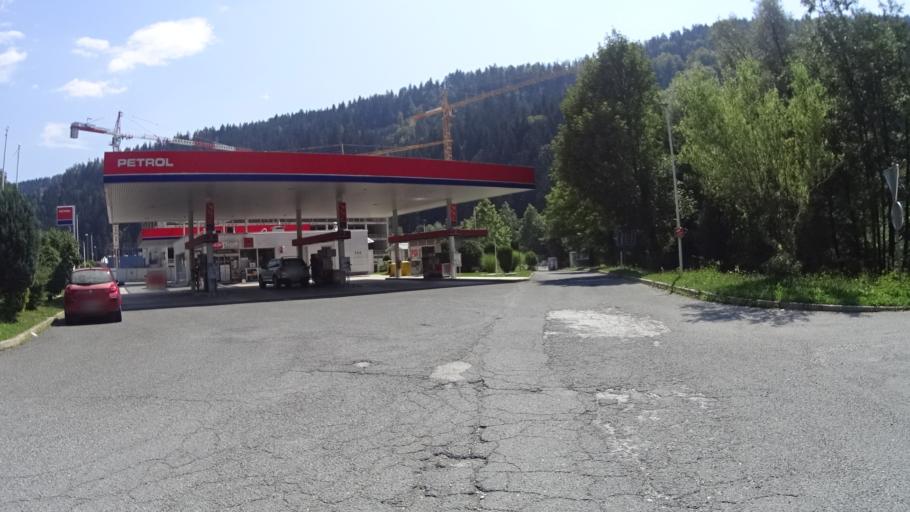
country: SI
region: Prevalje
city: Prevalje
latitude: 46.5431
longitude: 14.9035
